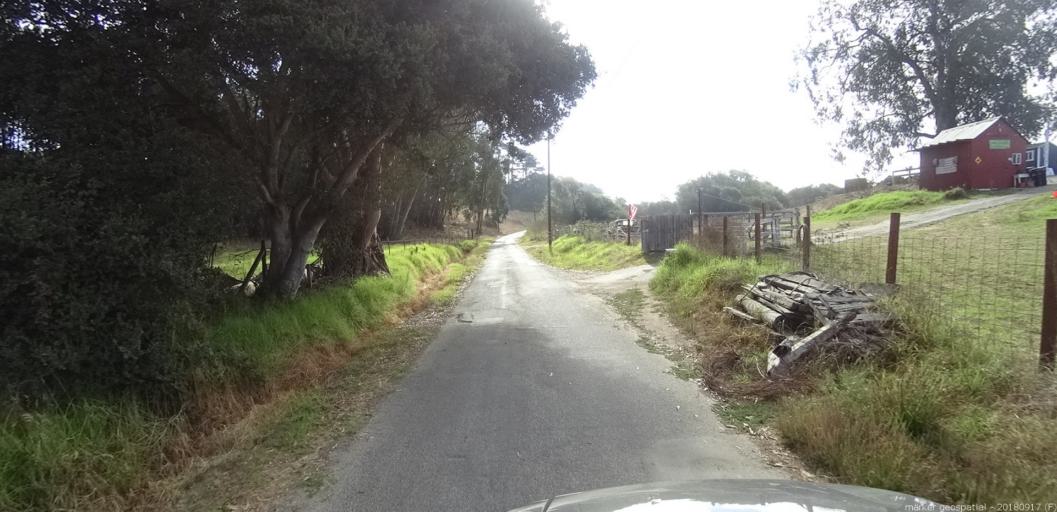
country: US
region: California
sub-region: Monterey County
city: Elkhorn
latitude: 36.7869
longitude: -121.7178
